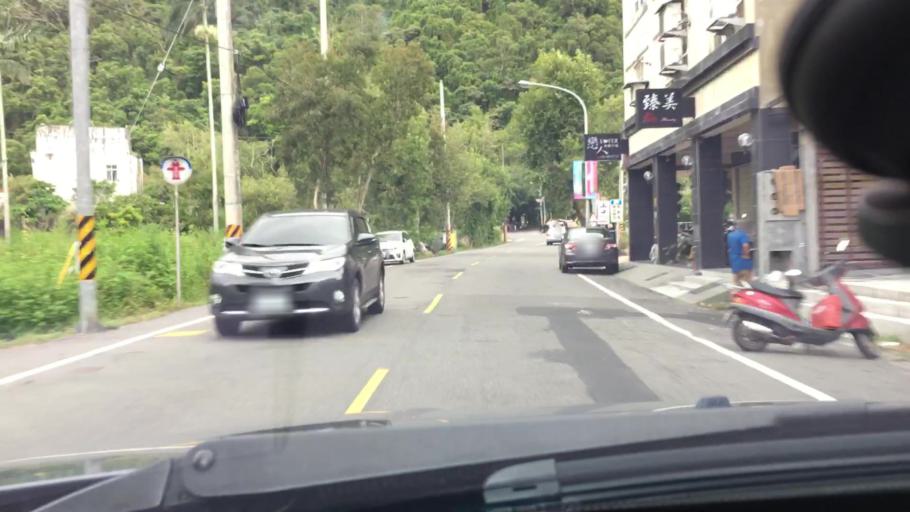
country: TW
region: Taiwan
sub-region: Yilan
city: Yilan
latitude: 24.8263
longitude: 121.7633
